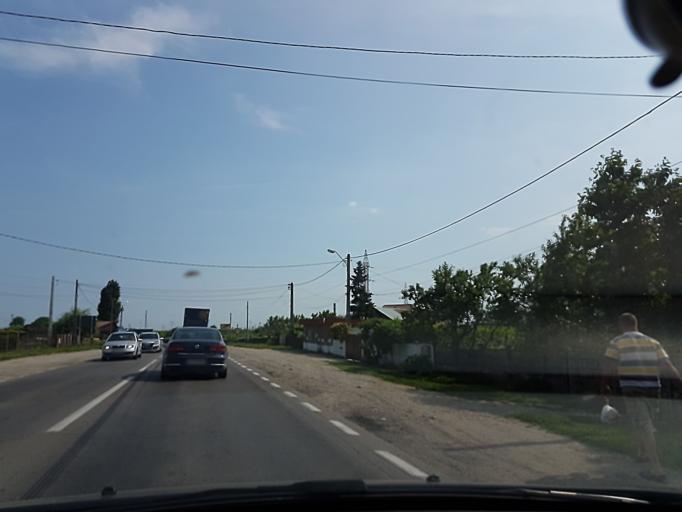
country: RO
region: Prahova
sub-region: Comuna Blejoiu
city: Blejoi
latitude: 45.0004
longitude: 26.0185
